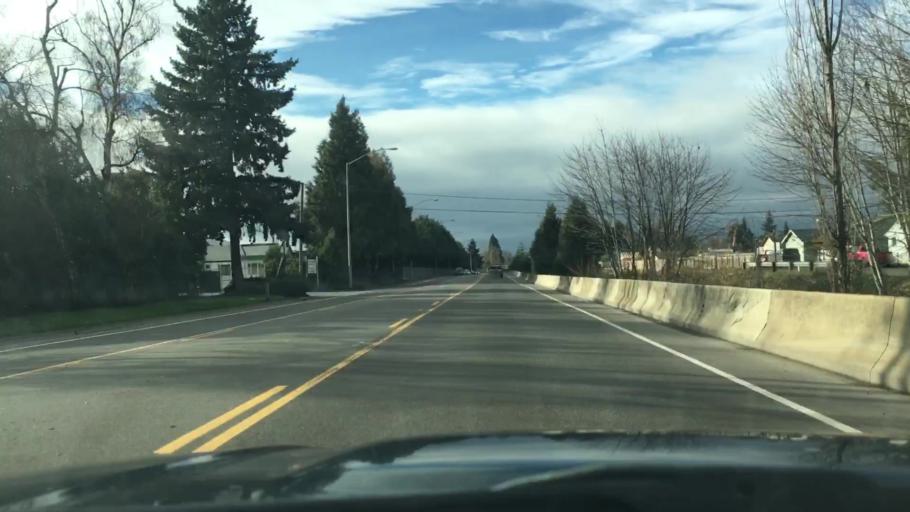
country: US
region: Oregon
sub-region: Lane County
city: Eugene
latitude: 44.0632
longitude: -123.1514
